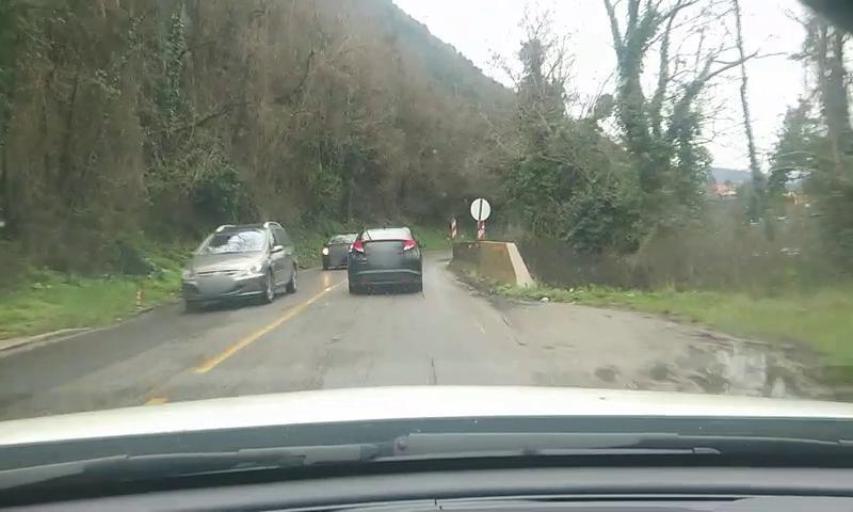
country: IT
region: Tuscany
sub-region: Provincia di Prato
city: Vaiano
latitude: 43.9276
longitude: 11.1268
